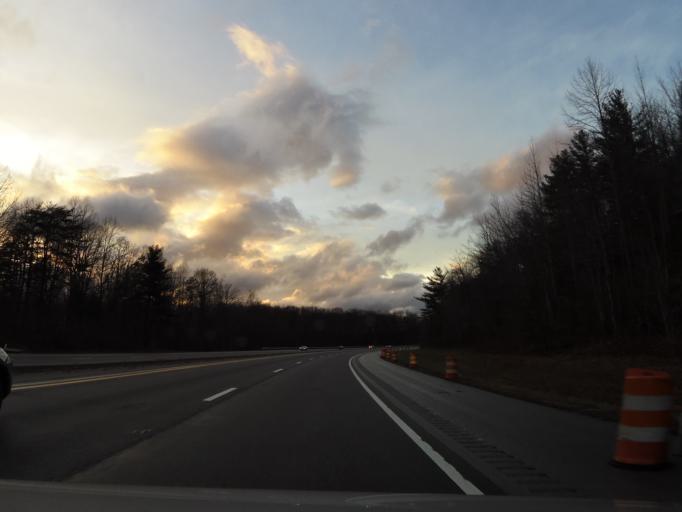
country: US
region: Tennessee
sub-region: Campbell County
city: Jacksboro
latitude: 36.4083
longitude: -84.2742
